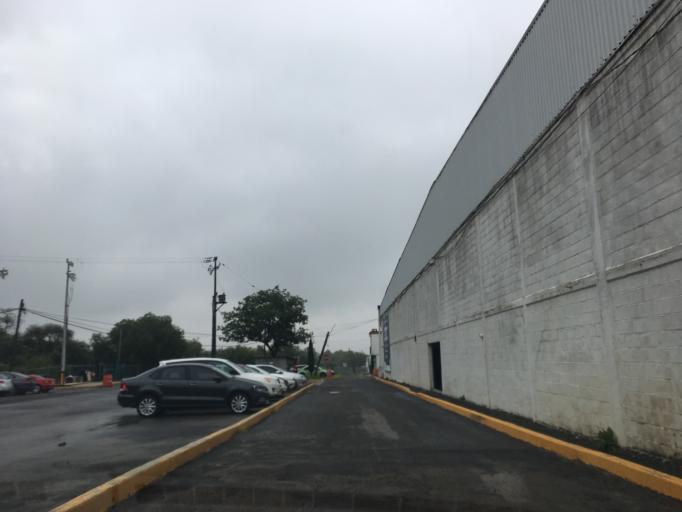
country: MX
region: Mexico
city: Ciudad Lopez Mateos
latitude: 19.5719
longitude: -99.2939
